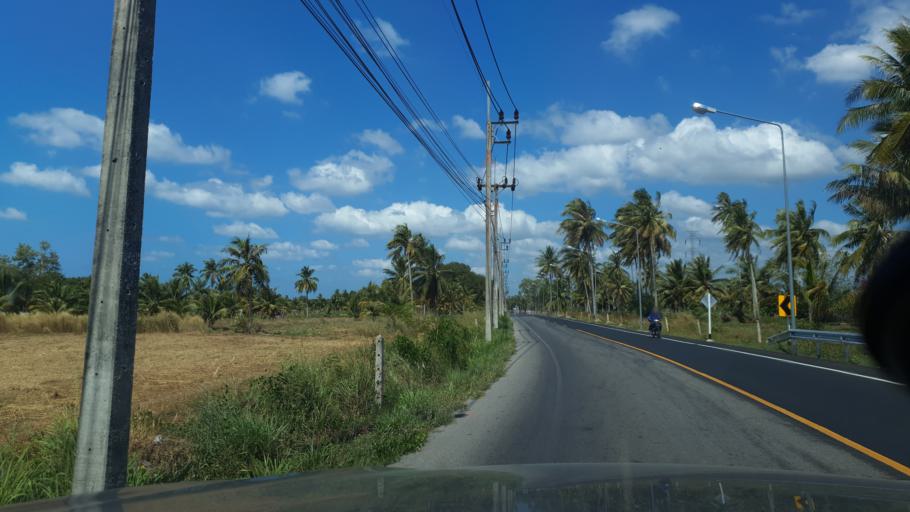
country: TH
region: Phuket
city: Thalang
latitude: 8.1453
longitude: 98.3060
